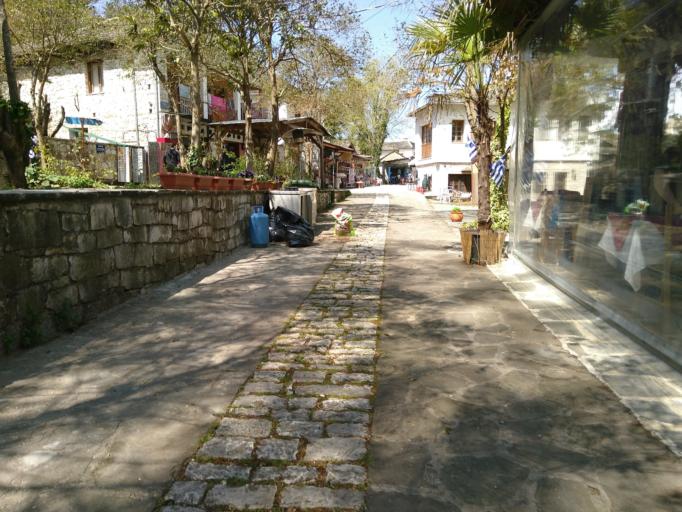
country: GR
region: Epirus
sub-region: Nomos Ioanninon
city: Ioannina
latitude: 39.6794
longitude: 20.8760
